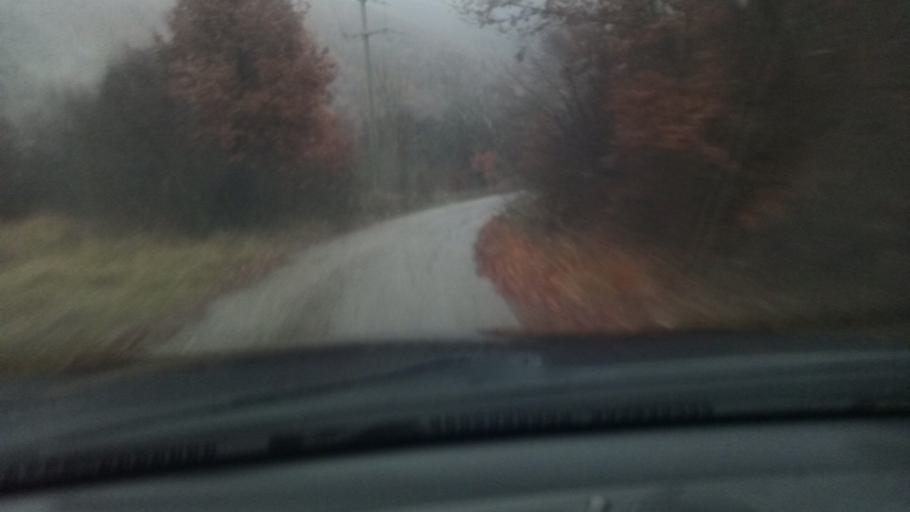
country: MK
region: Vinica
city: Blatec
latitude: 41.8406
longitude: 22.6136
